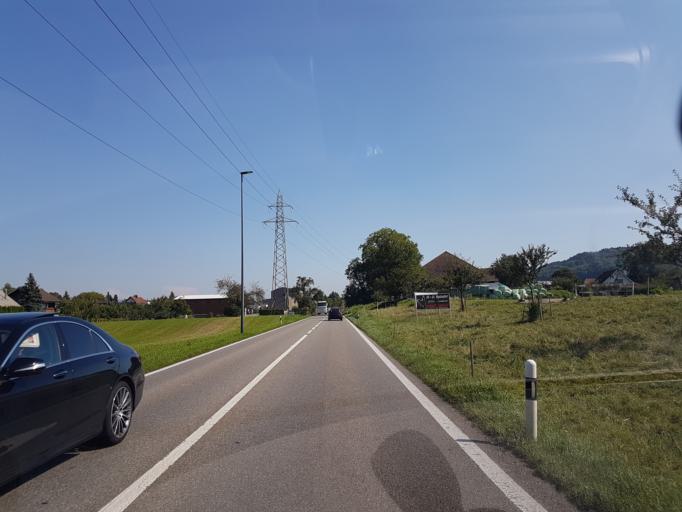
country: CH
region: Aargau
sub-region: Bezirk Bremgarten
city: Wohlen
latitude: 47.3419
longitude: 8.2706
